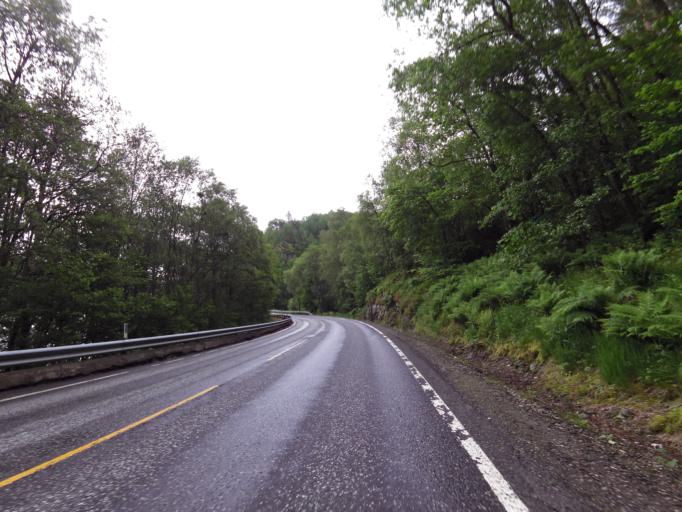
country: NO
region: Vest-Agder
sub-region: Farsund
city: Farsund
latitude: 58.1023
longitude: 6.9019
